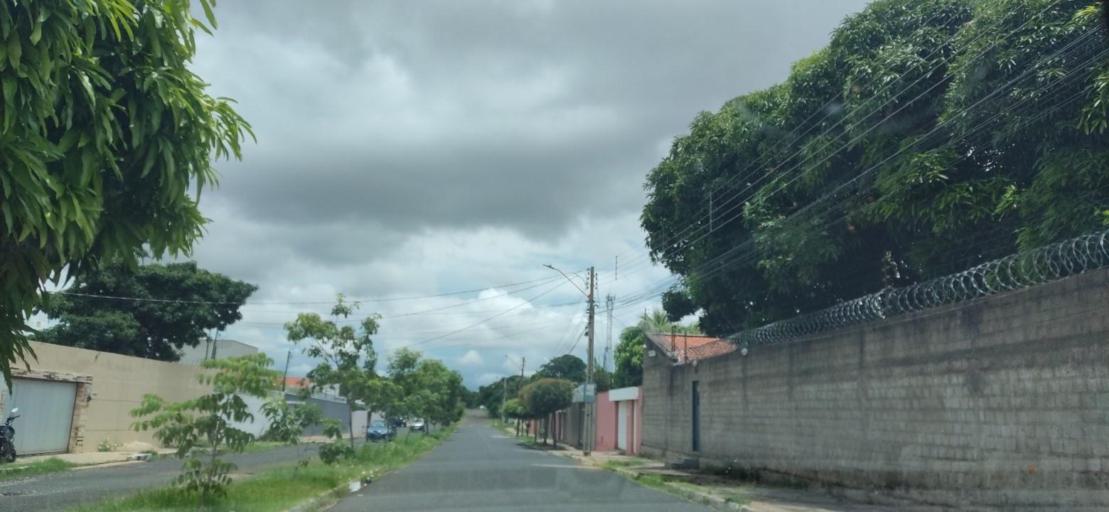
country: BR
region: Piaui
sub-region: Teresina
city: Teresina
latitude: -5.0747
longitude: -42.7587
